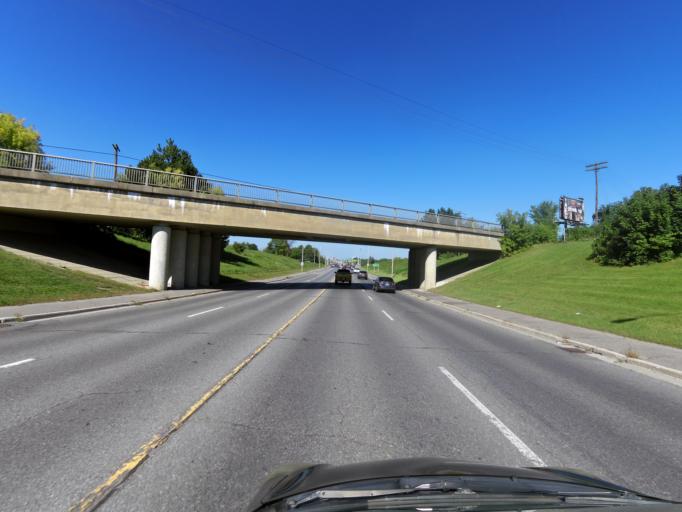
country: CA
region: Ontario
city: Bells Corners
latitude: 45.3305
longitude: -75.8156
